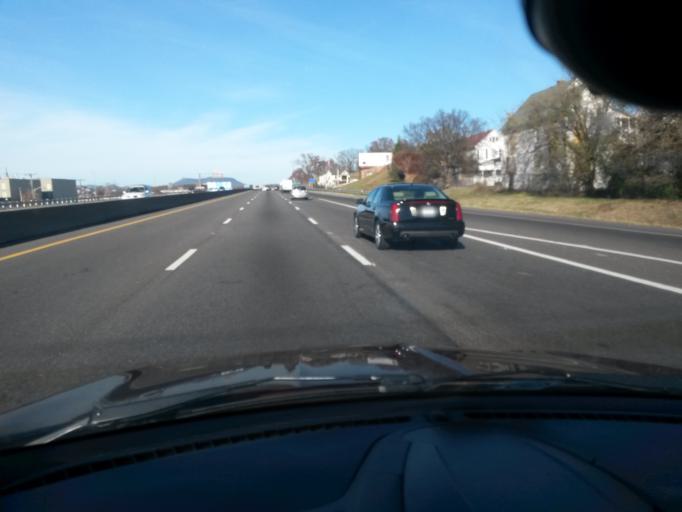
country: US
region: Virginia
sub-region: City of Roanoke
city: Cedar Bluff
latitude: 37.2682
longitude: -79.9367
